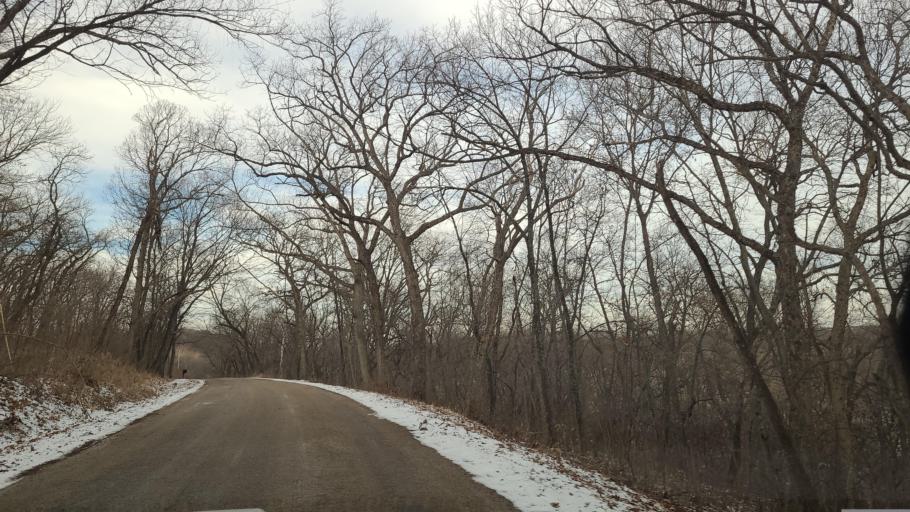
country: US
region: Kansas
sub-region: Shawnee County
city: Topeka
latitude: 39.0513
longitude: -95.5035
